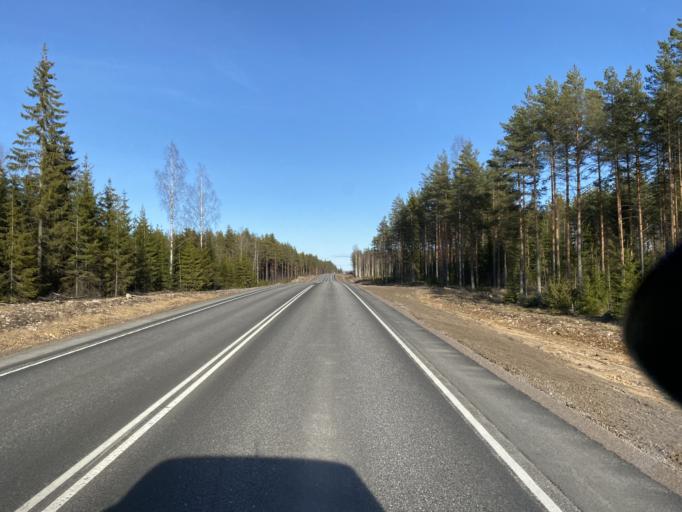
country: FI
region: Satakunta
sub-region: Pori
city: Kokemaeki
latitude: 61.1697
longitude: 22.4647
